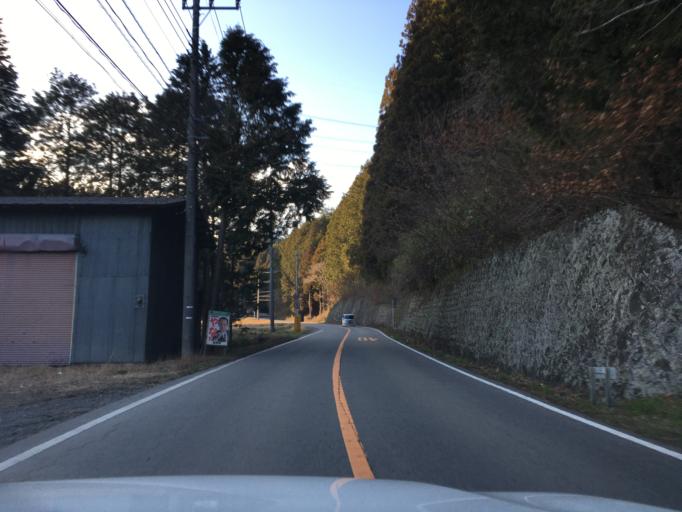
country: JP
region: Tochigi
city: Otawara
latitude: 36.8453
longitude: 140.1862
